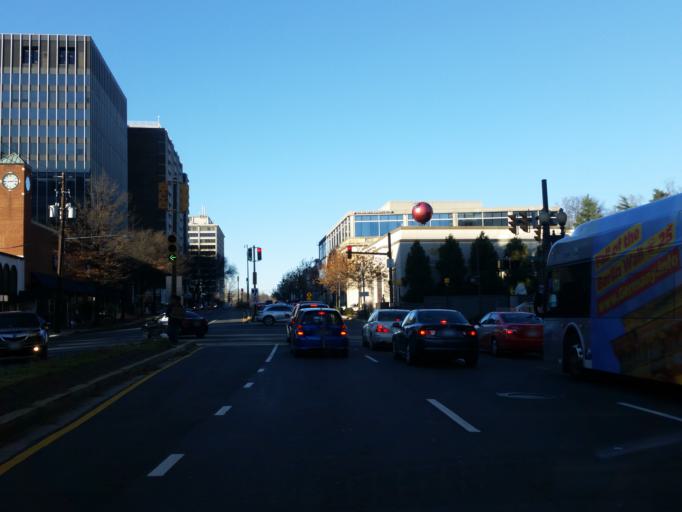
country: US
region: Maryland
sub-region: Montgomery County
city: Friendship Village
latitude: 38.9616
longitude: -77.0860
